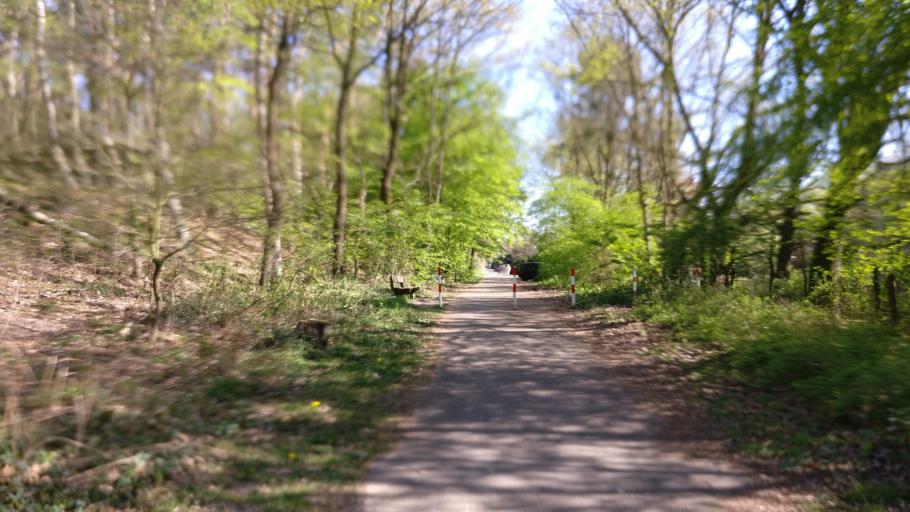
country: DE
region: North Rhine-Westphalia
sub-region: Regierungsbezirk Detmold
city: Lage
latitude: 52.0107
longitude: 8.7676
